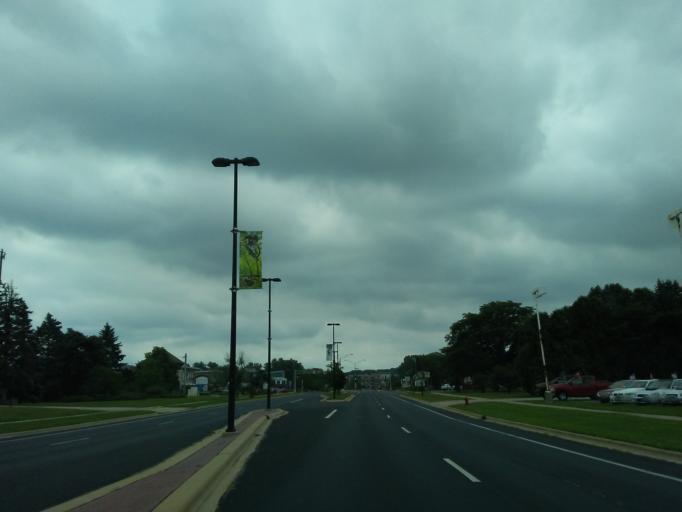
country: US
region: Wisconsin
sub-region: Dane County
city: Middleton
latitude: 43.1077
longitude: -89.5104
